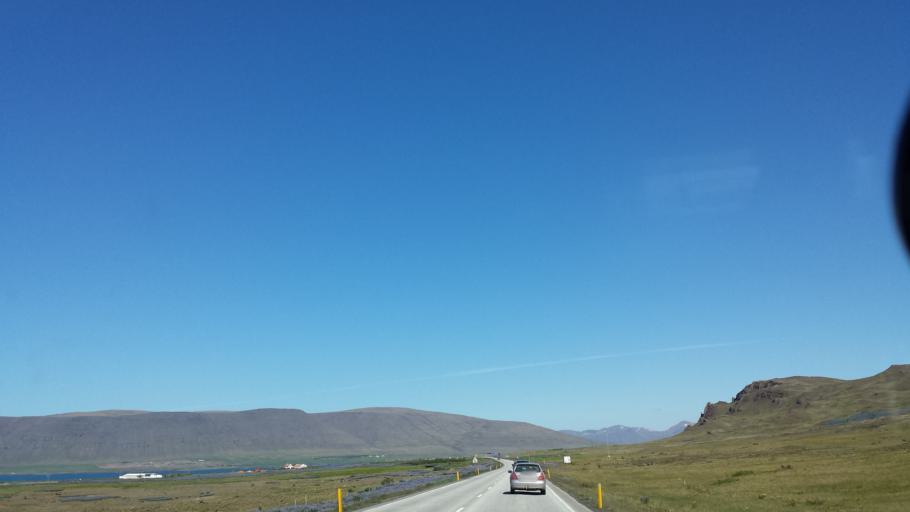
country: IS
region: Capital Region
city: Reykjavik
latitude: 64.2628
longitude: -21.8333
